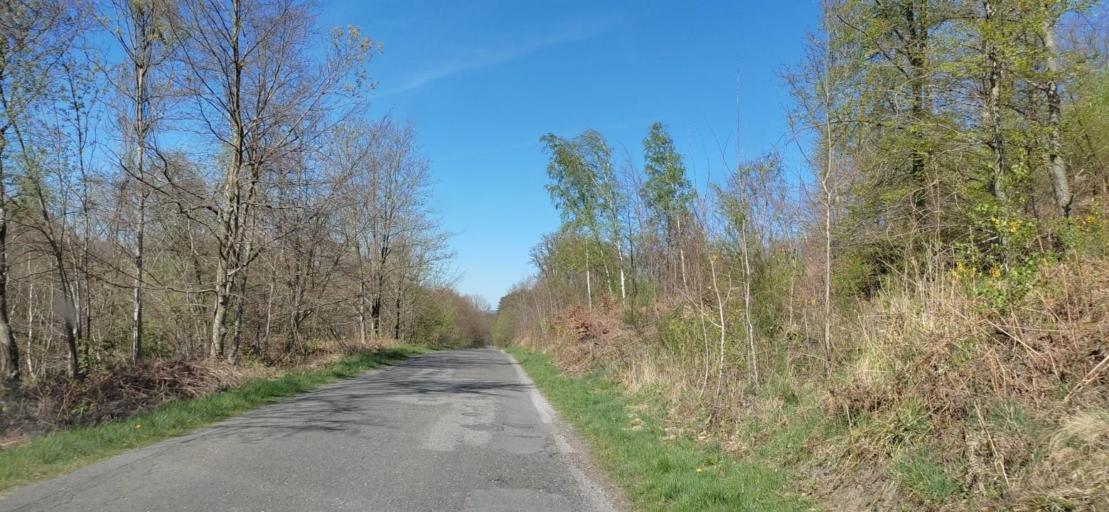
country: FR
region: Picardie
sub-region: Departement de l'Oise
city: Le Plessis-Brion
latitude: 49.4475
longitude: 2.9209
